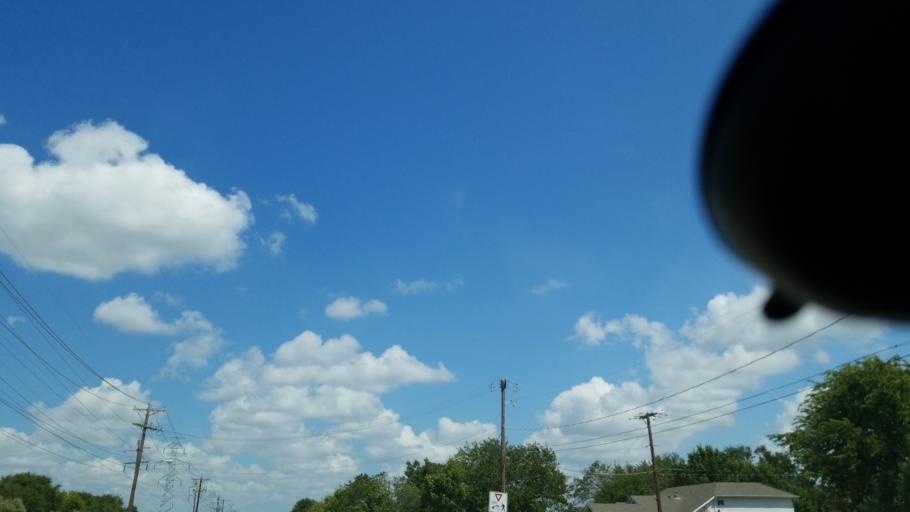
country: US
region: Texas
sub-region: Dallas County
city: Grand Prairie
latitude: 32.7243
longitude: -96.9858
